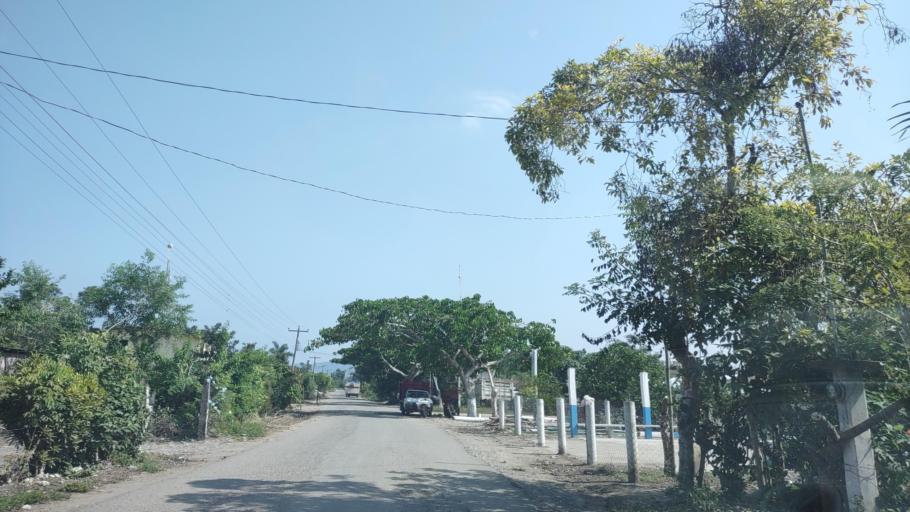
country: MX
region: Puebla
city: Espinal
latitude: 20.2546
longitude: -97.3309
